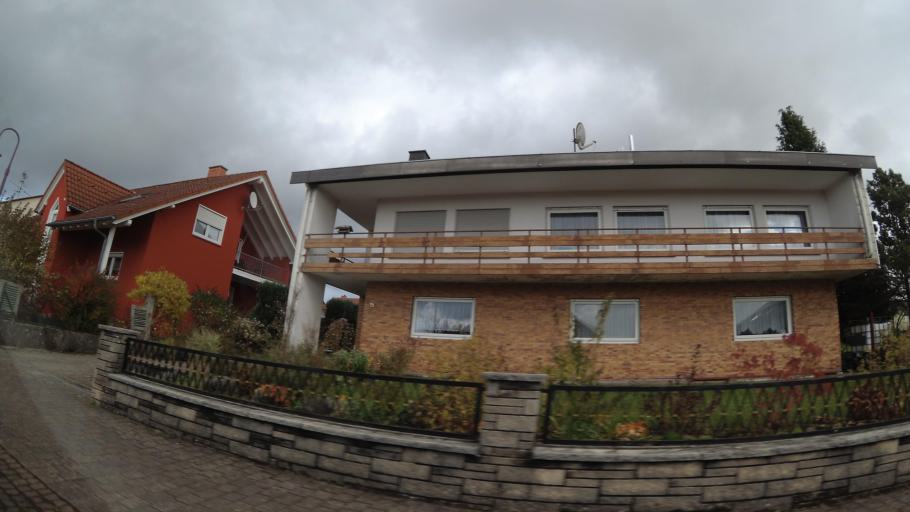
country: DE
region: Rheinland-Pfalz
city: Bottenbach
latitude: 49.1796
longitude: 7.4993
